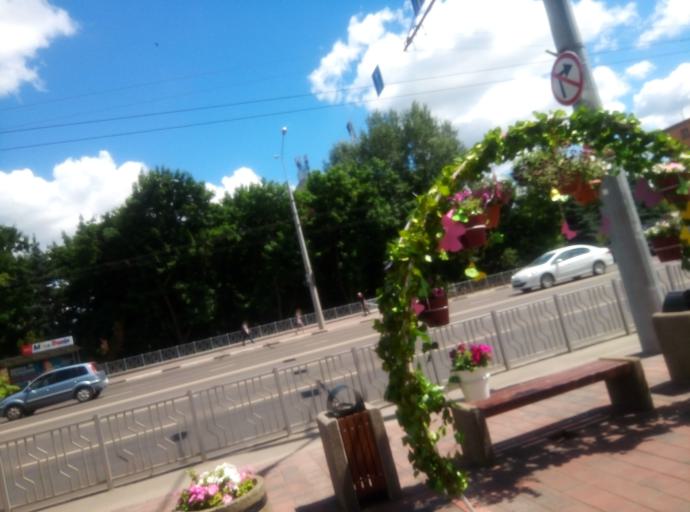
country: RU
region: Kursk
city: Kursk
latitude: 51.7612
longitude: 36.1857
